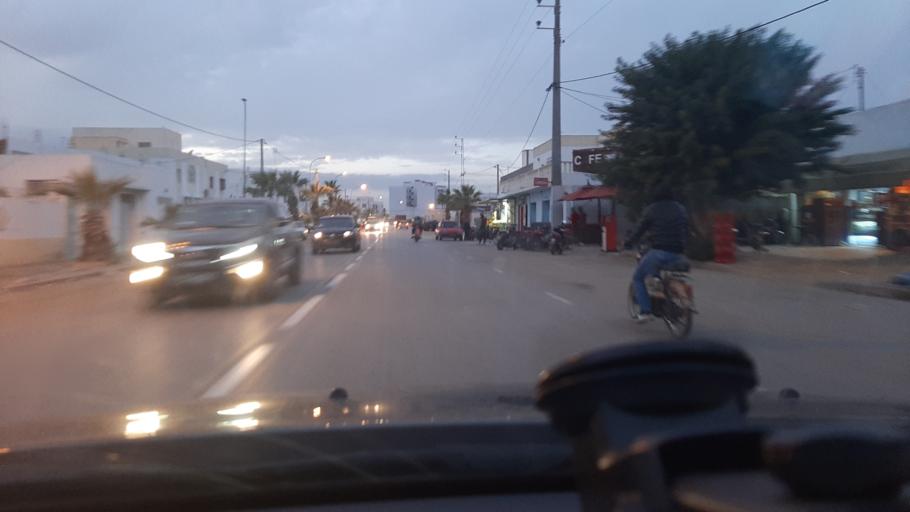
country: TN
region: Safaqis
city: Sfax
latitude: 34.7629
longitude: 10.6914
